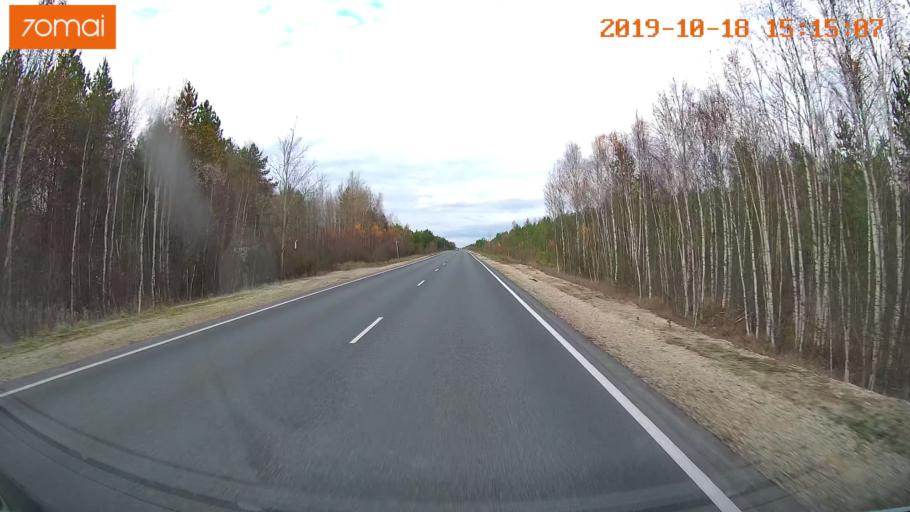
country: RU
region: Vladimir
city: Gus'-Khrustal'nyy
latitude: 55.6138
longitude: 40.7217
